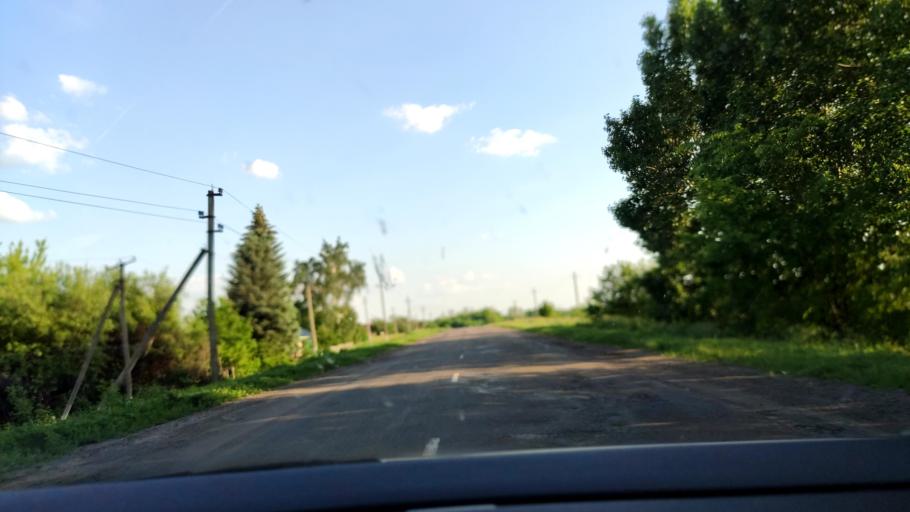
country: RU
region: Voronezj
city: Kashirskoye
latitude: 51.5078
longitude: 39.8323
